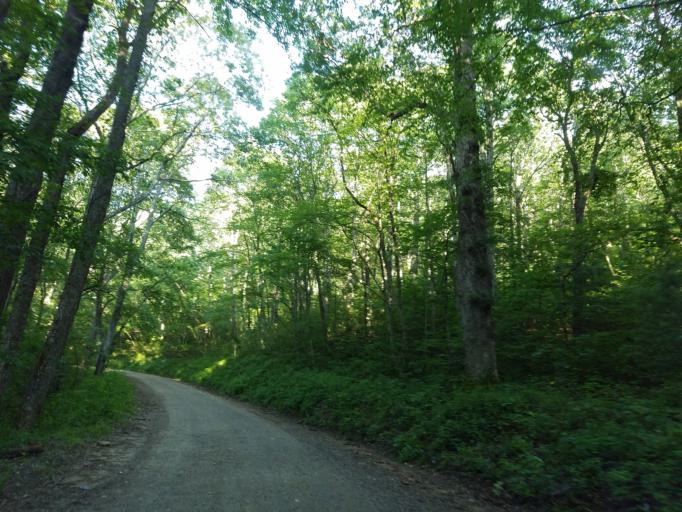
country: US
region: Georgia
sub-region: Lumpkin County
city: Dahlonega
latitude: 34.6557
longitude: -84.1051
